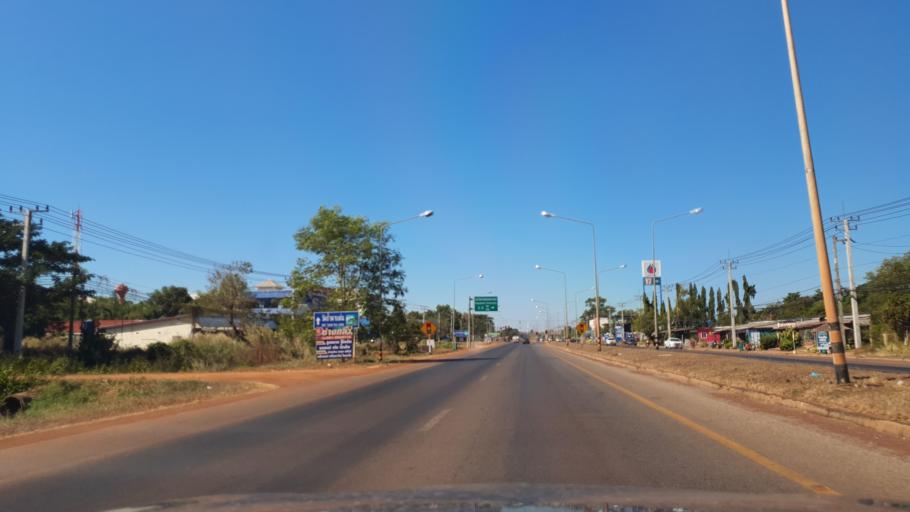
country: TH
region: Sakon Nakhon
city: Sakon Nakhon
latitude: 17.2634
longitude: 104.1372
